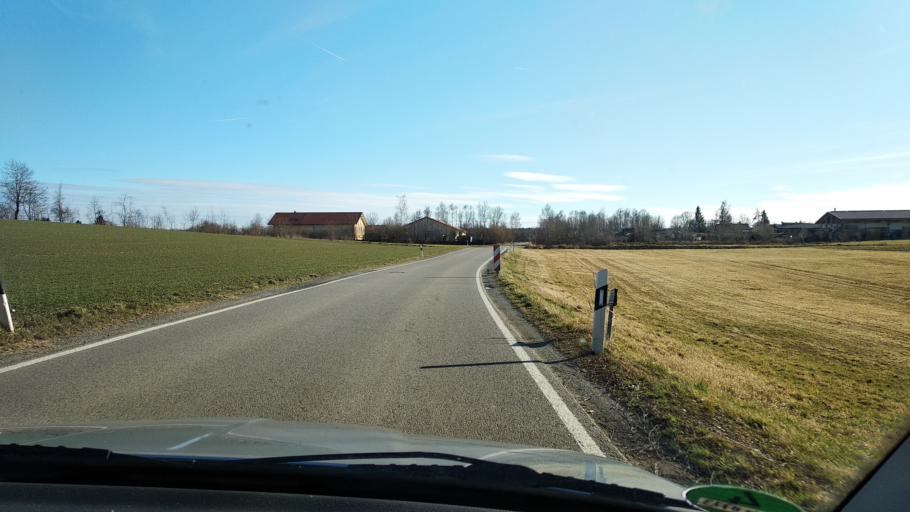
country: DE
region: Bavaria
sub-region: Upper Bavaria
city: Egmating
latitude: 48.0087
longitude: 11.8001
